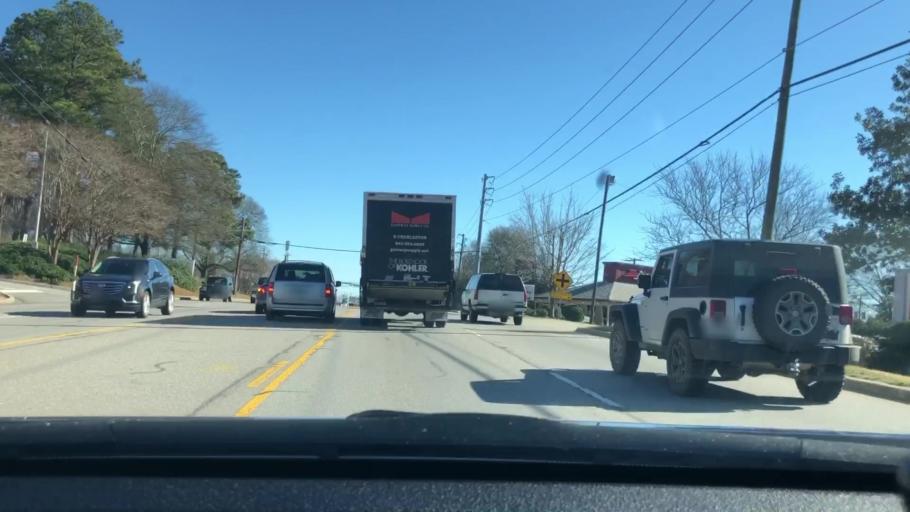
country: US
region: South Carolina
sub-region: Lexington County
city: Oak Grove
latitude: 34.0044
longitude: -81.1147
